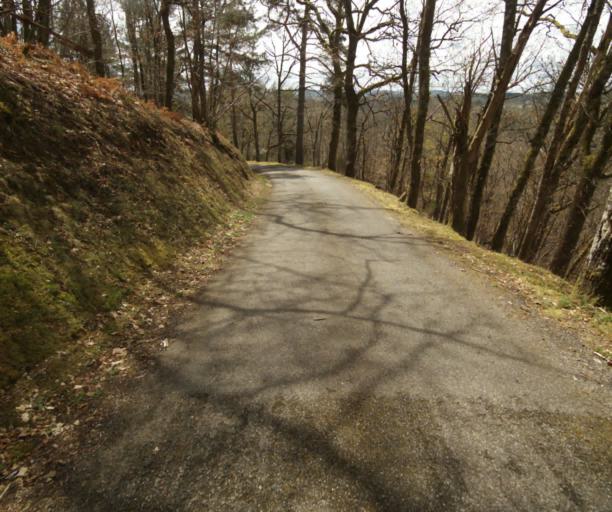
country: FR
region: Limousin
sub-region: Departement de la Correze
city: Sainte-Fortunade
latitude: 45.1953
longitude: 1.8779
